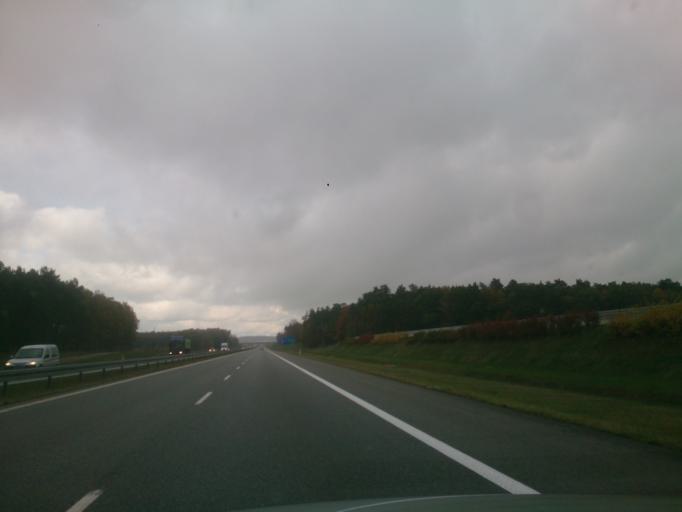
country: PL
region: Pomeranian Voivodeship
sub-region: Powiat tczewski
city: Pelplin
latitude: 54.0112
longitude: 18.6616
